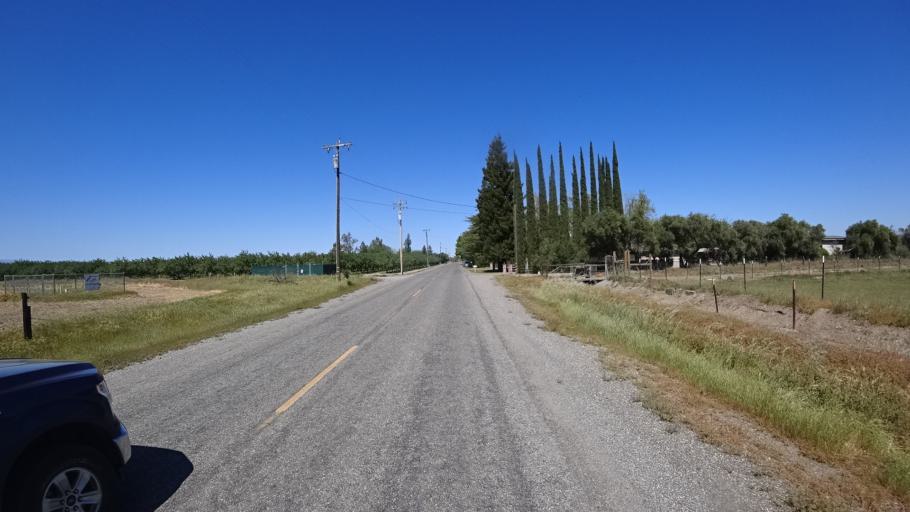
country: US
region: California
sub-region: Glenn County
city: Orland
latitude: 39.7360
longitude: -122.1594
